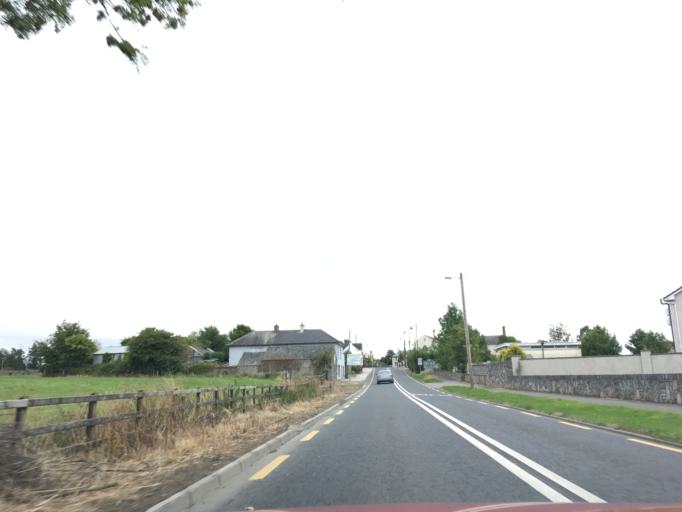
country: IE
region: Munster
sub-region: South Tipperary
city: Cluain Meala
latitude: 52.4138
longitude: -7.7571
